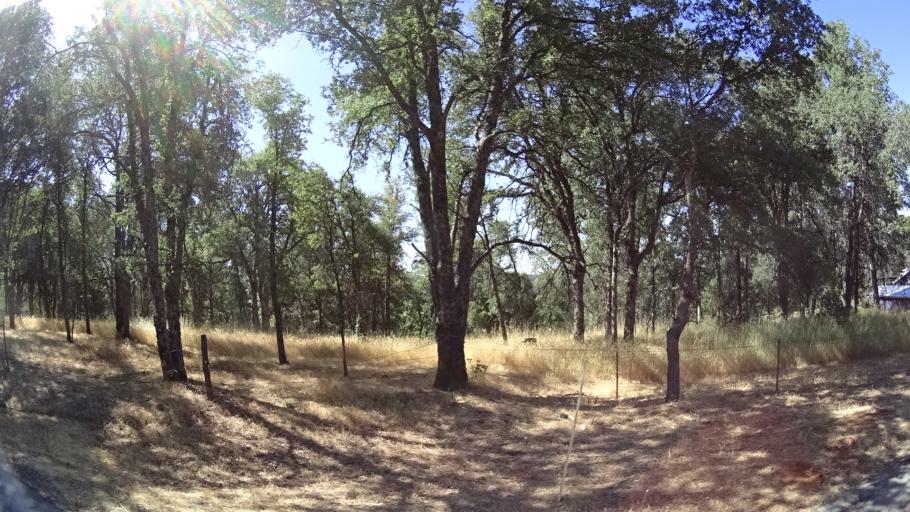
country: US
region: California
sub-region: Amador County
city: Pioneer
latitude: 38.3938
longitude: -120.4751
